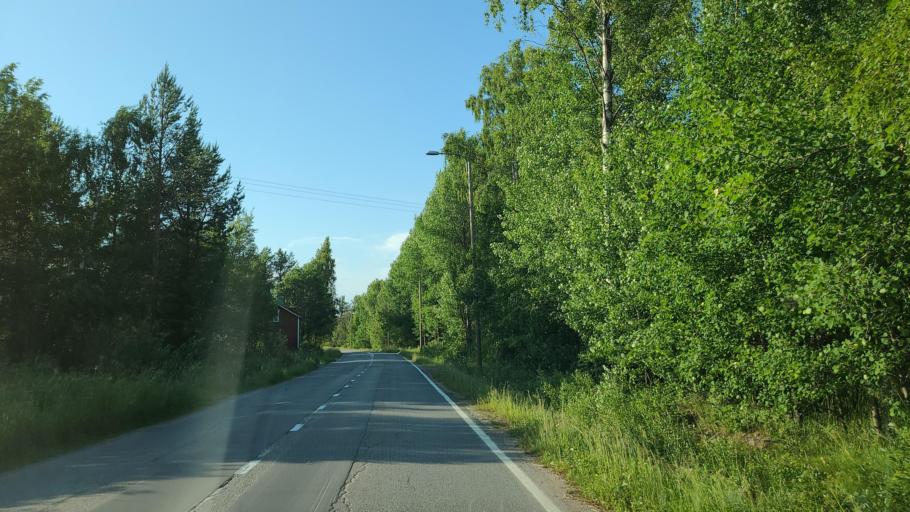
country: FI
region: Ostrobothnia
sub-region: Vaasa
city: Replot
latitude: 63.3395
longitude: 21.3310
